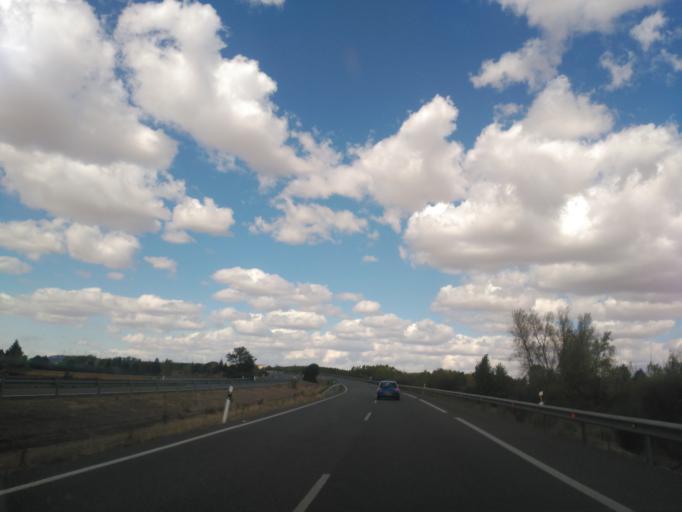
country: ES
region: Castille and Leon
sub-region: Provincia de Palencia
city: Venta de Banos
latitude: 41.9261
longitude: -4.5005
